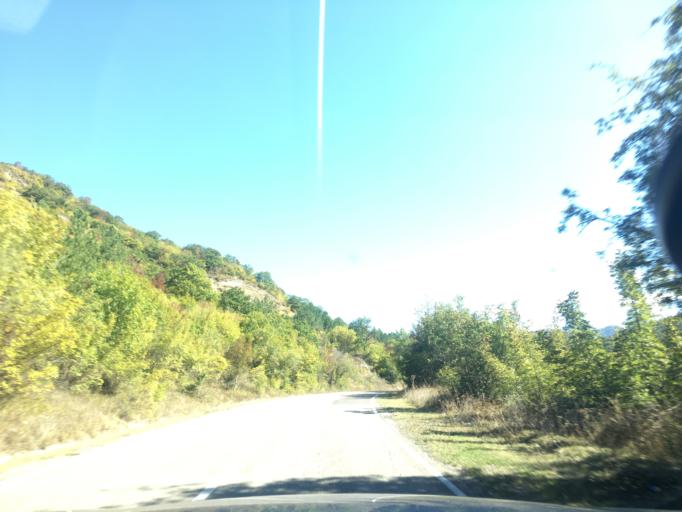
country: GE
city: Didi Lilo
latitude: 41.8539
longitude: 44.8930
